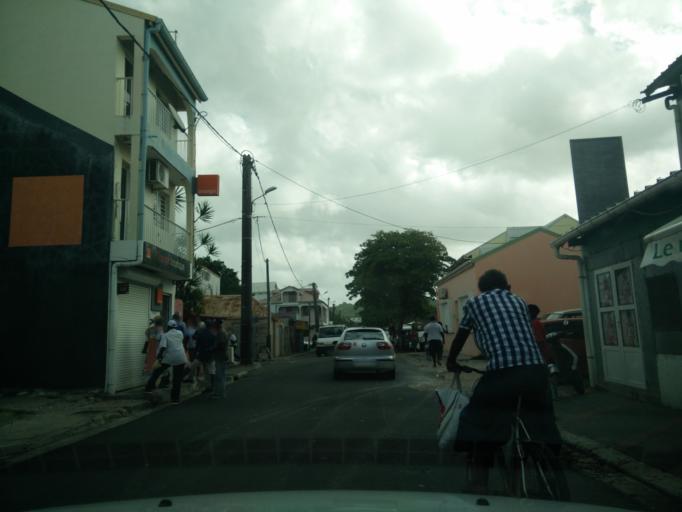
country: GP
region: Guadeloupe
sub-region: Guadeloupe
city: Grand-Bourg
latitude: 15.8822
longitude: -61.3144
